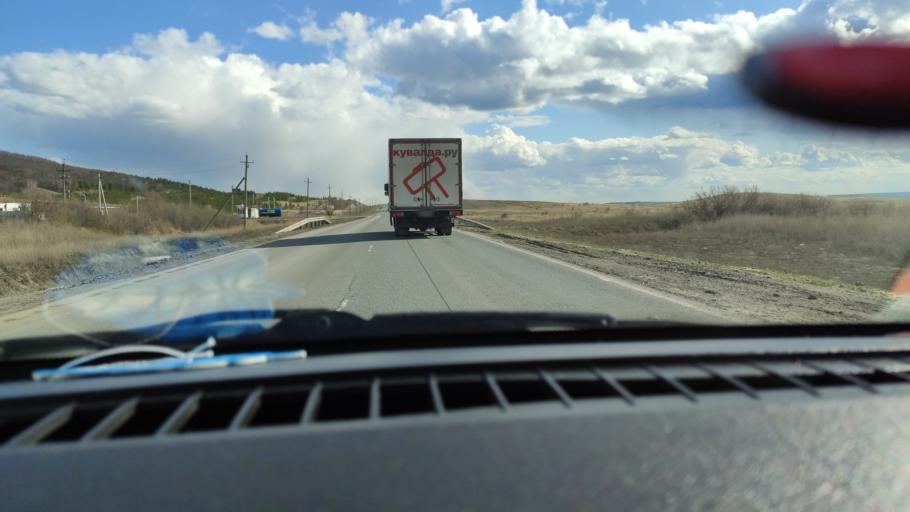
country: RU
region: Saratov
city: Alekseyevka
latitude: 52.3040
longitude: 47.9263
